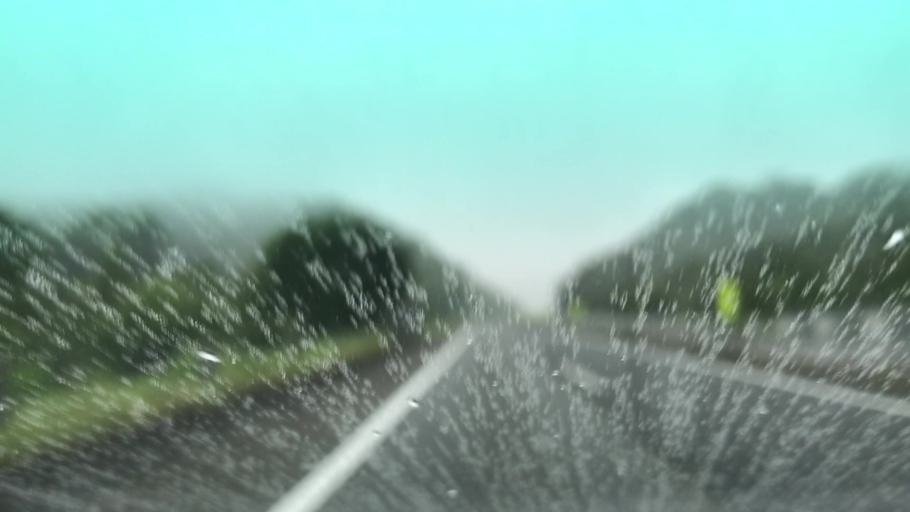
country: JP
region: Hokkaido
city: Shiraoi
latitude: 42.5587
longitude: 141.3176
